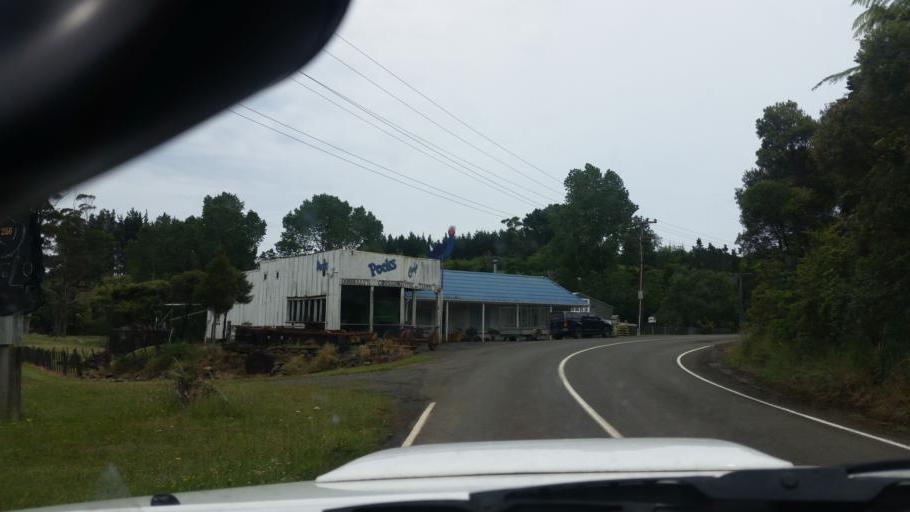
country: NZ
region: Northland
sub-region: Kaipara District
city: Dargaville
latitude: -35.7106
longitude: 173.6182
